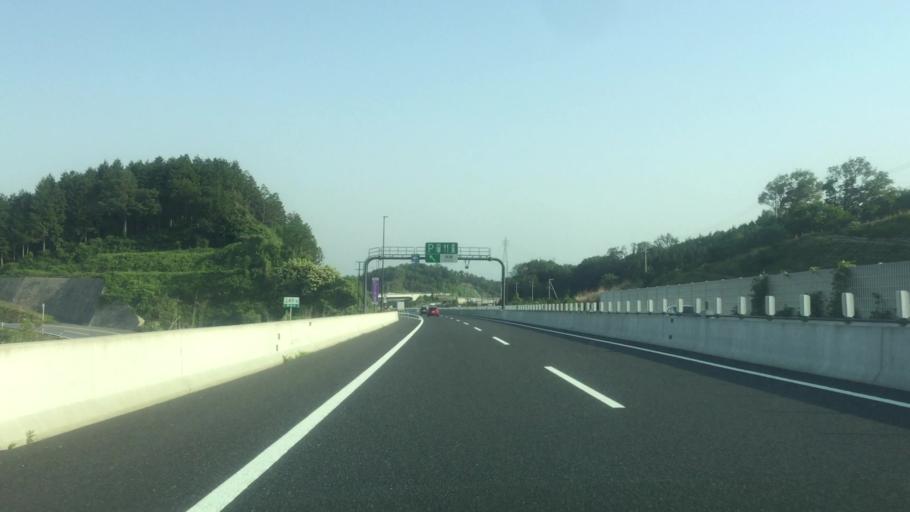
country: JP
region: Aichi
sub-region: Toyota-shi
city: Toyota
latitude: 35.0274
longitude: 137.2239
